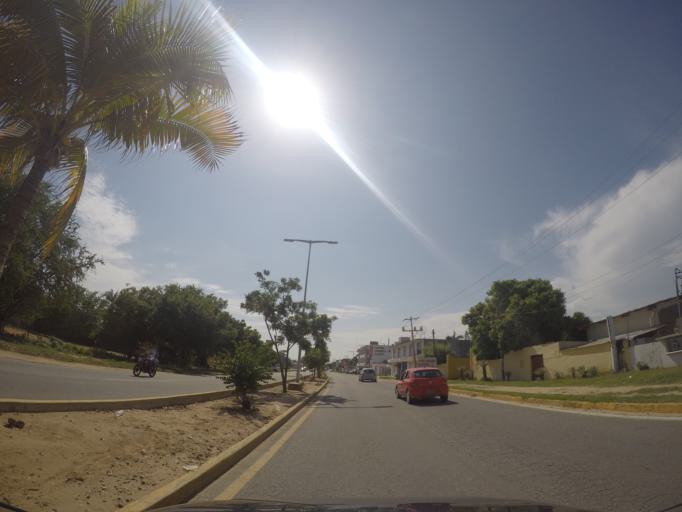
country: MX
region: Oaxaca
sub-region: San Pedro Mixtepec -Dto. 22 -
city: Puerto Escondido
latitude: 15.8665
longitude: -97.0770
